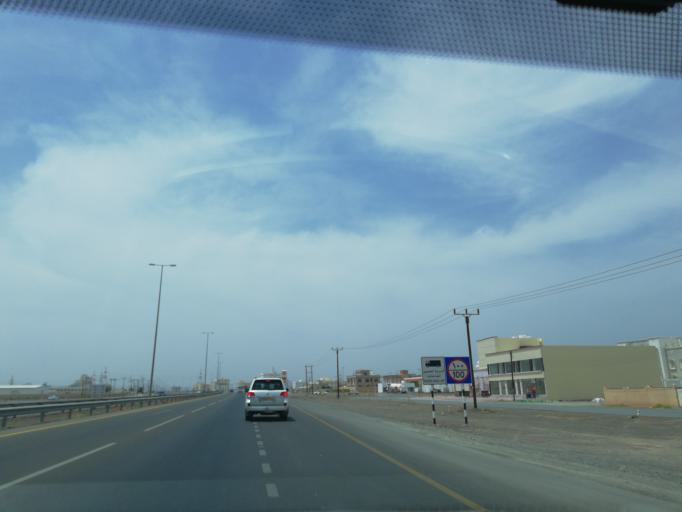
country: OM
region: Muhafazat ad Dakhiliyah
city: Nizwa
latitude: 22.8586
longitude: 57.5209
